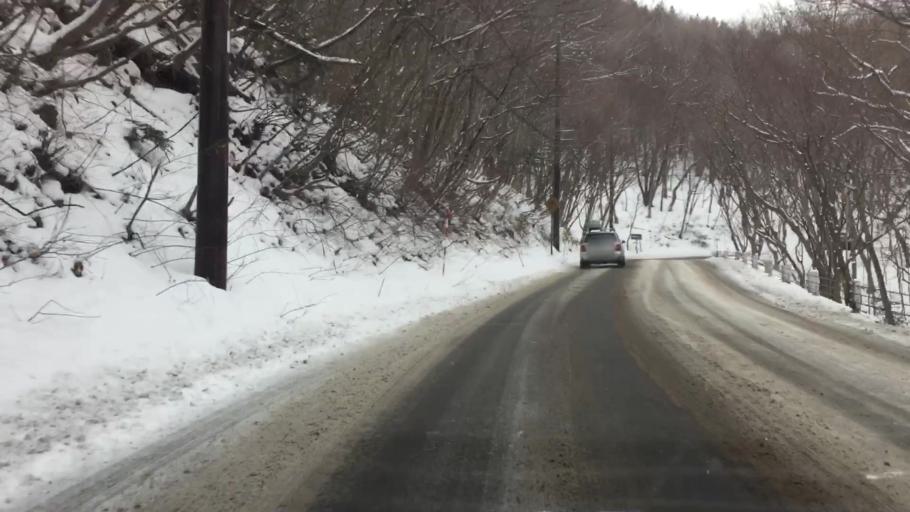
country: JP
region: Tochigi
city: Yaita
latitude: 36.9693
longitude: 139.7927
